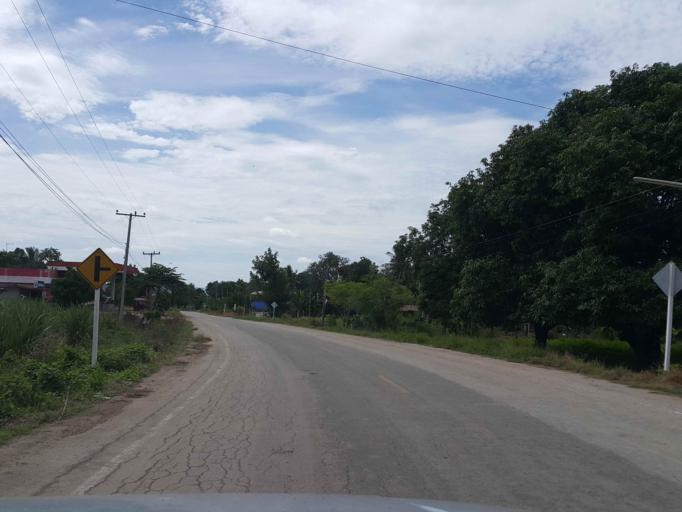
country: TH
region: Sukhothai
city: Ban Dan Lan Hoi
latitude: 17.0769
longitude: 99.4797
